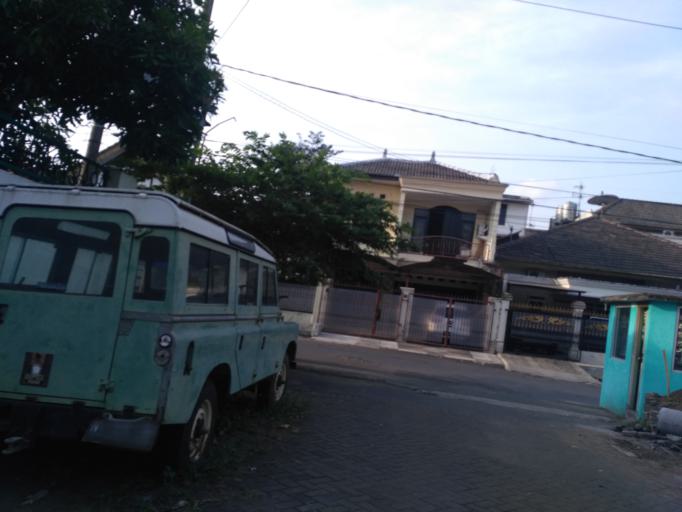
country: ID
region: East Java
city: Malang
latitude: -7.9371
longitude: 112.6367
